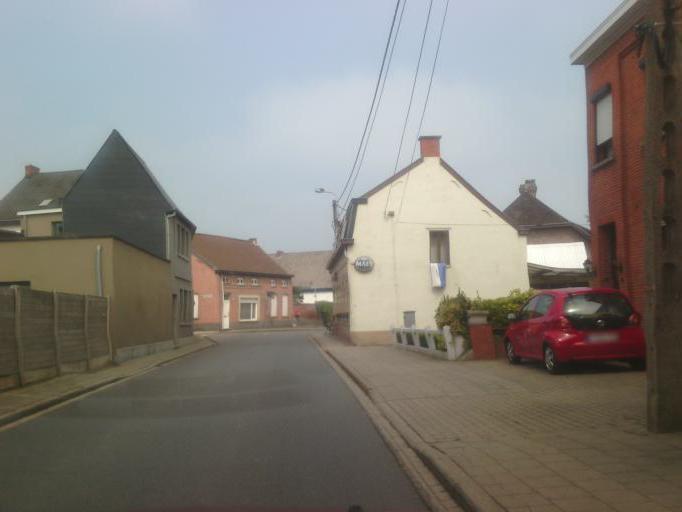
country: BE
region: Flanders
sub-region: Provincie Oost-Vlaanderen
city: Berlare
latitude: 51.0033
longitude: 4.0157
